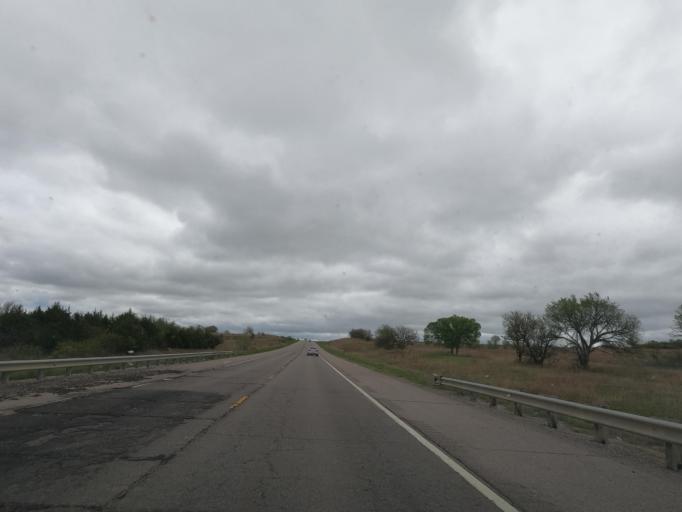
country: US
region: Kansas
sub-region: Elk County
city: Howard
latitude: 37.6363
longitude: -96.3498
